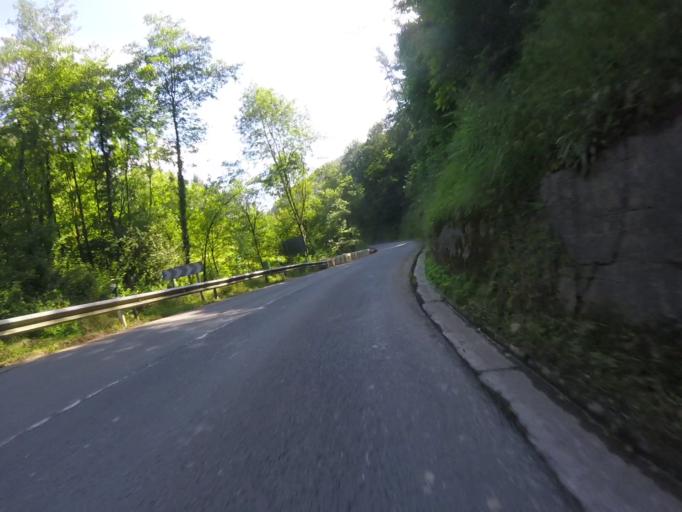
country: ES
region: Basque Country
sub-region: Provincia de Guipuzcoa
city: Beizama
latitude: 43.1000
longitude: -2.2440
